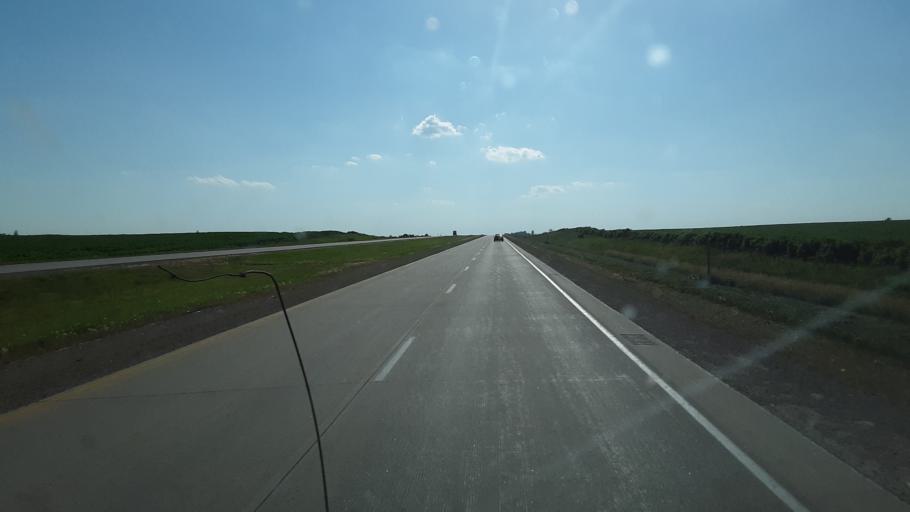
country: US
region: Iowa
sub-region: Grundy County
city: Dike
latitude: 42.4638
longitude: -92.6943
